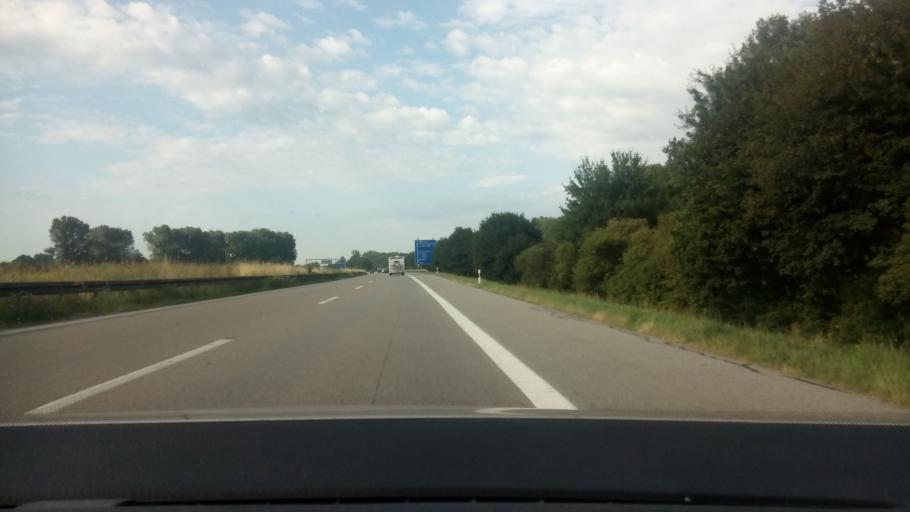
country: DE
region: Bavaria
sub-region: Upper Bavaria
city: Oberschleissheim
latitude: 48.2602
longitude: 11.5348
